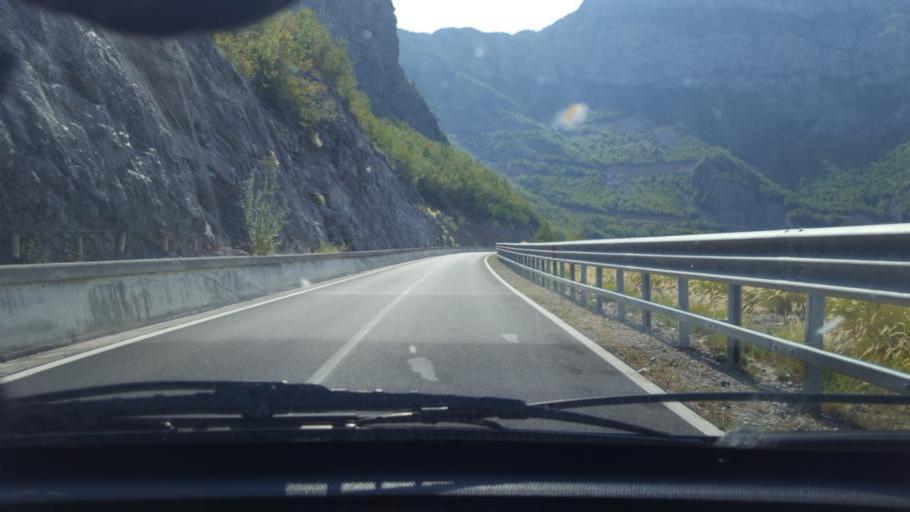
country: AL
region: Shkoder
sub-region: Rrethi i Malesia e Madhe
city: Kastrat
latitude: 42.4196
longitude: 19.5028
